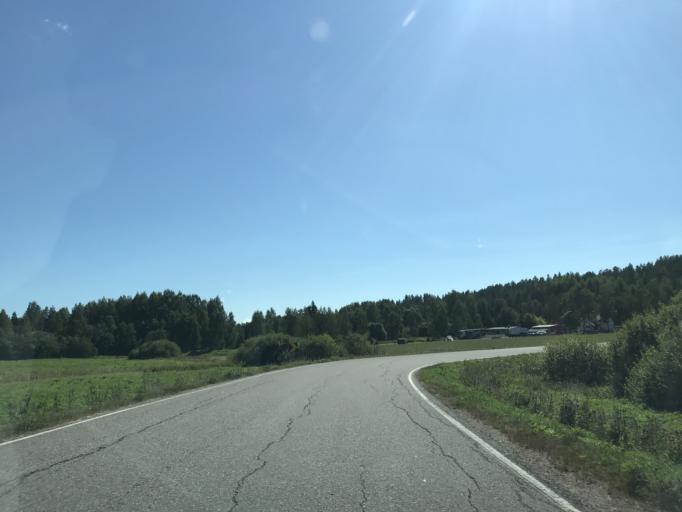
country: FI
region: Paijanne Tavastia
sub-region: Lahti
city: Orimattila
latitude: 60.8027
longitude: 25.6925
